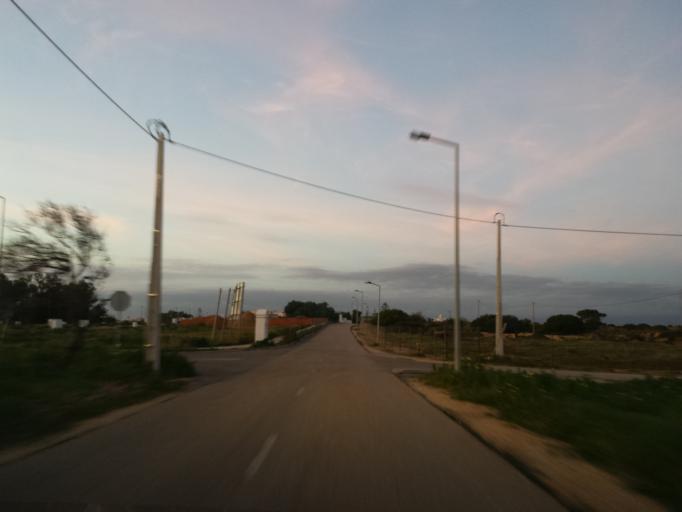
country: PT
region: Faro
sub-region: Lagos
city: Lagos
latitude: 37.0863
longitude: -8.6710
